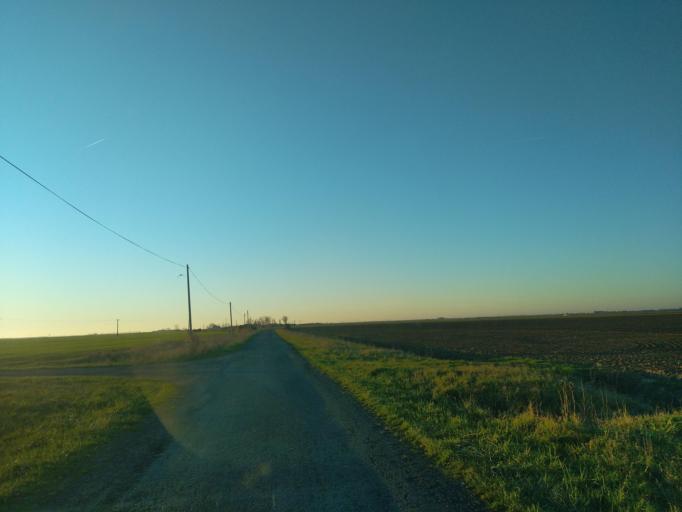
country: FR
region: Pays de la Loire
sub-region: Departement de la Vendee
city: Triaize
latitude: 46.3707
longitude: -1.2665
